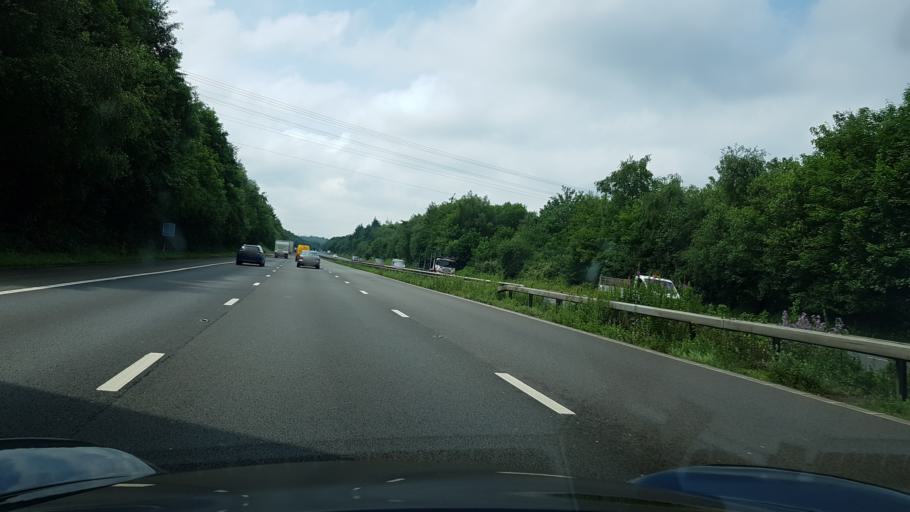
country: GB
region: England
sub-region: West Sussex
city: Maidenbower
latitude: 51.1035
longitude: -0.1454
